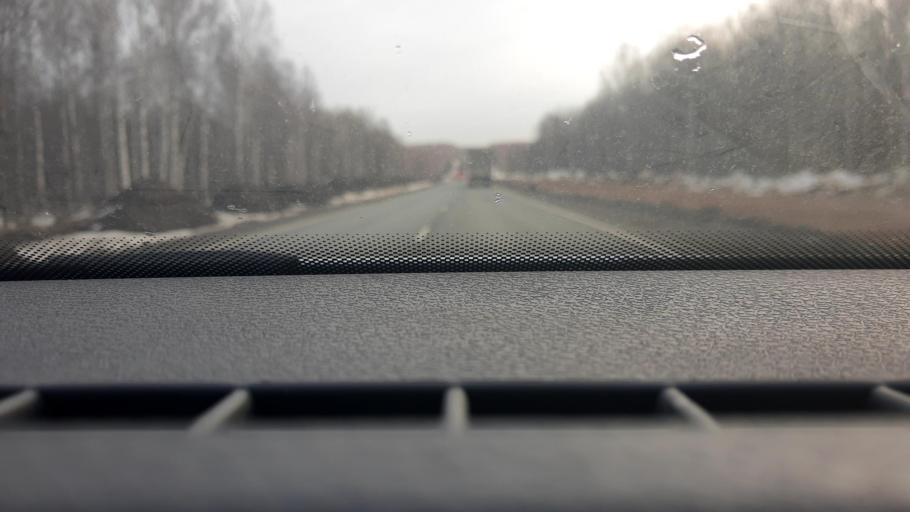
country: RU
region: Chelyabinsk
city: Asha
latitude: 54.8678
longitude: 57.1755
